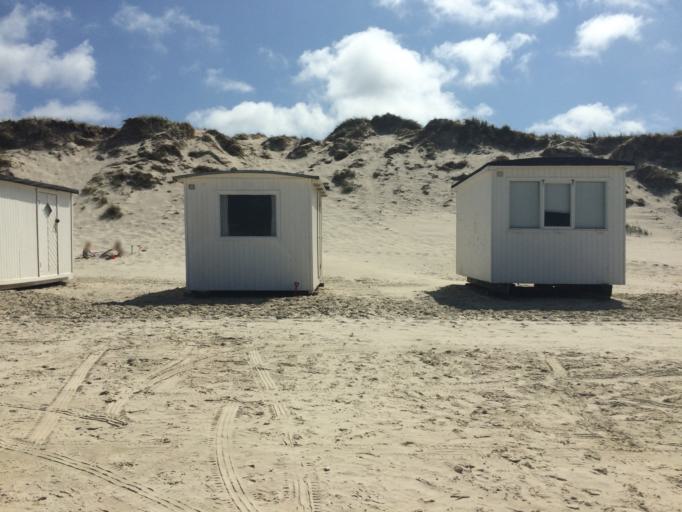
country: DK
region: North Denmark
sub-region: Jammerbugt Kommune
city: Pandrup
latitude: 57.2530
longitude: 9.5770
